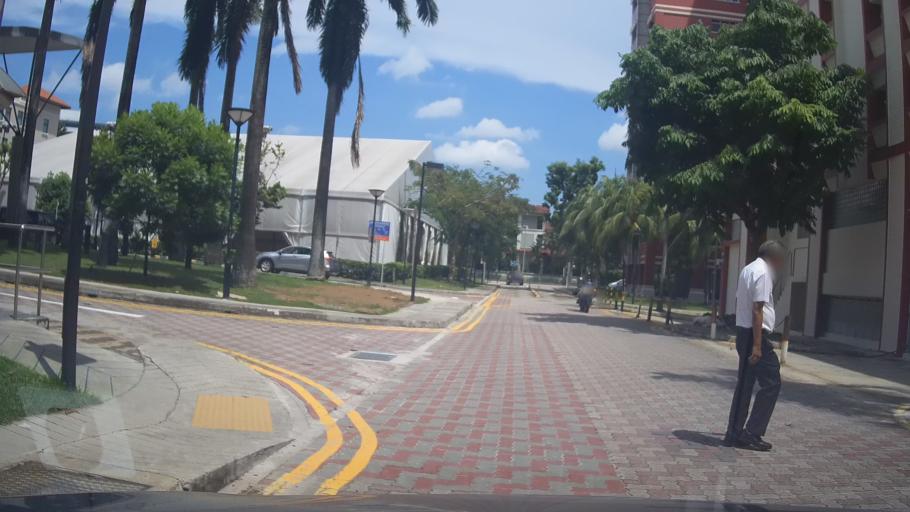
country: MY
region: Johor
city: Kampung Pasir Gudang Baru
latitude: 1.3774
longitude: 103.9429
